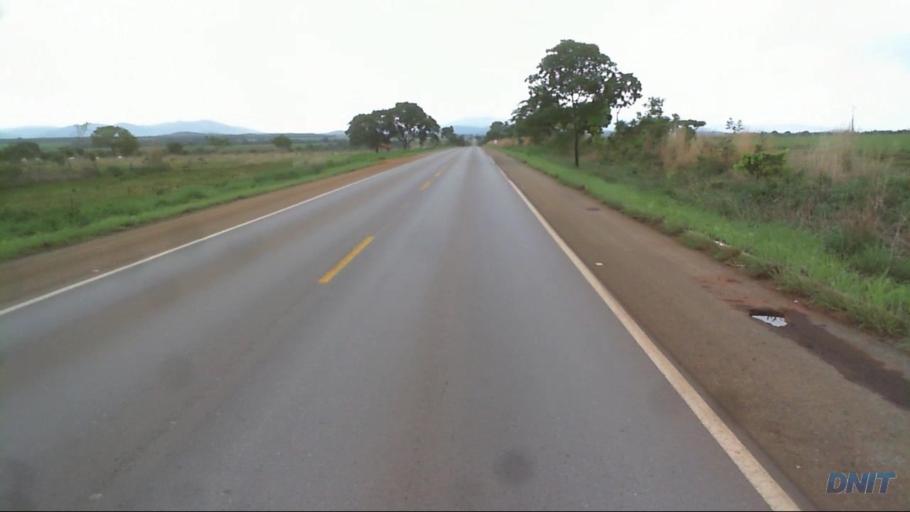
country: BR
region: Goias
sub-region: Barro Alto
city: Barro Alto
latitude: -14.7974
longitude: -49.0502
